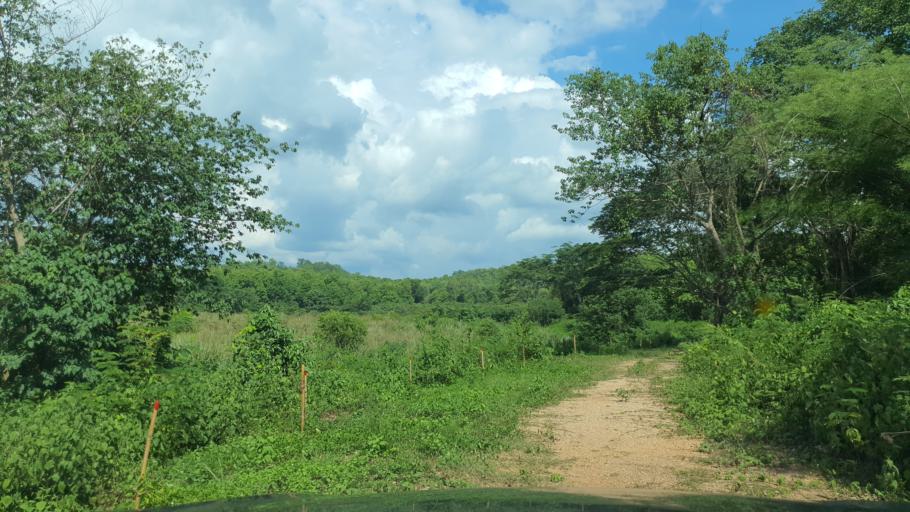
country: TH
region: Chiang Mai
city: Mae Taeng
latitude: 19.0913
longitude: 99.0799
